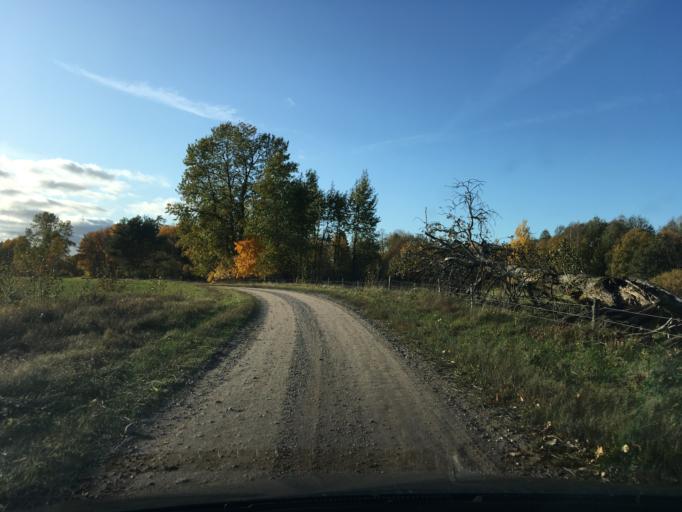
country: EE
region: Laeaene
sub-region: Lihula vald
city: Lihula
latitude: 58.5654
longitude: 23.7859
